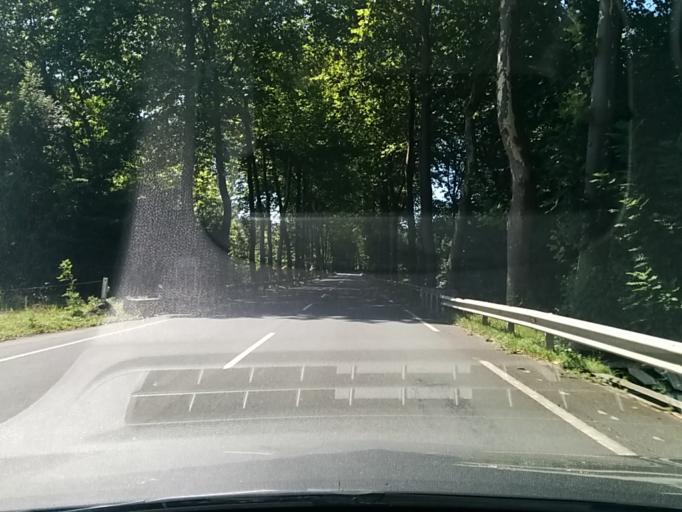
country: ES
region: Basque Country
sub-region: Provincia de Guipuzcoa
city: Zumaia
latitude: 43.2767
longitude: -2.2793
